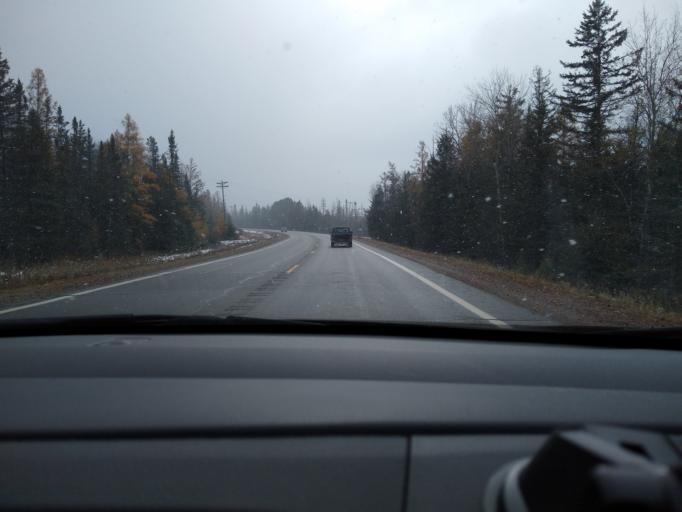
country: US
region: Wisconsin
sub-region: Florence County
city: Florence
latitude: 46.0715
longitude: -88.0770
